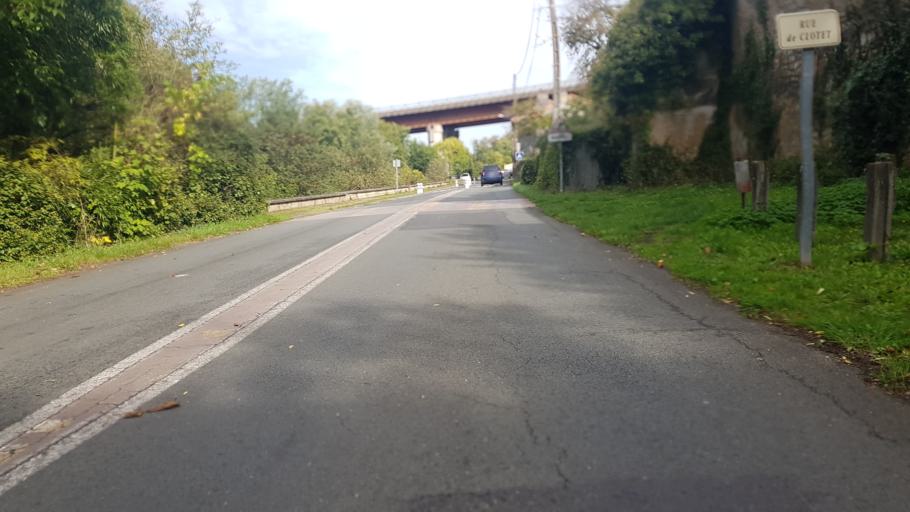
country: FR
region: Poitou-Charentes
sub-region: Departement de la Vienne
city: Chasseneuil-du-Poitou
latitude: 46.6167
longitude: 0.3590
